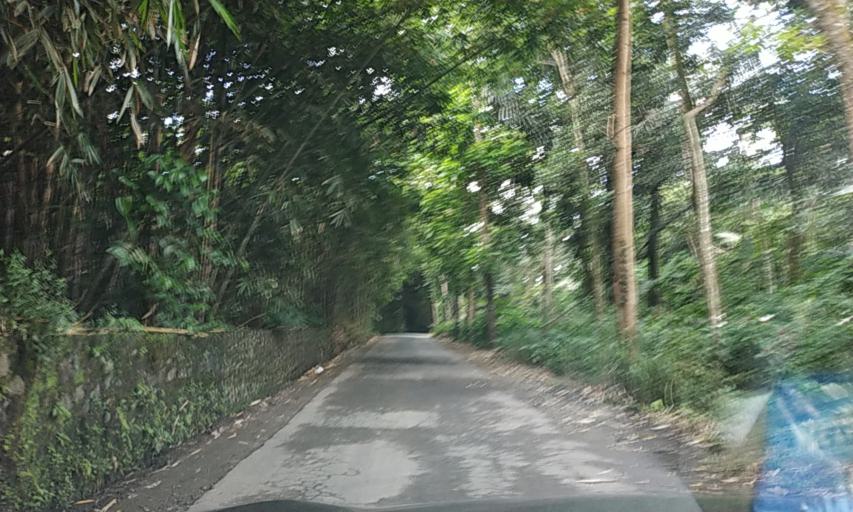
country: ID
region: Central Java
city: Jogonalan
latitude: -7.6288
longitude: 110.4722
